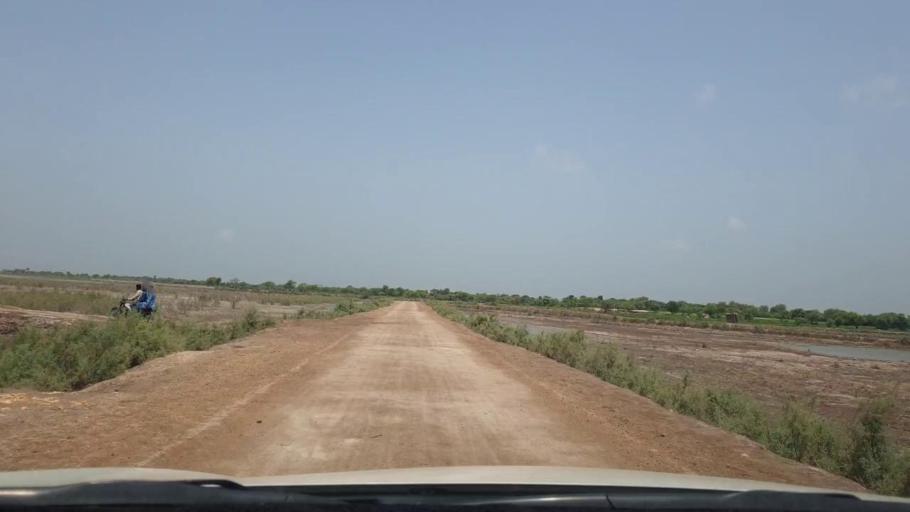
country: PK
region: Sindh
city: Talhar
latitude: 24.9245
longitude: 68.8329
